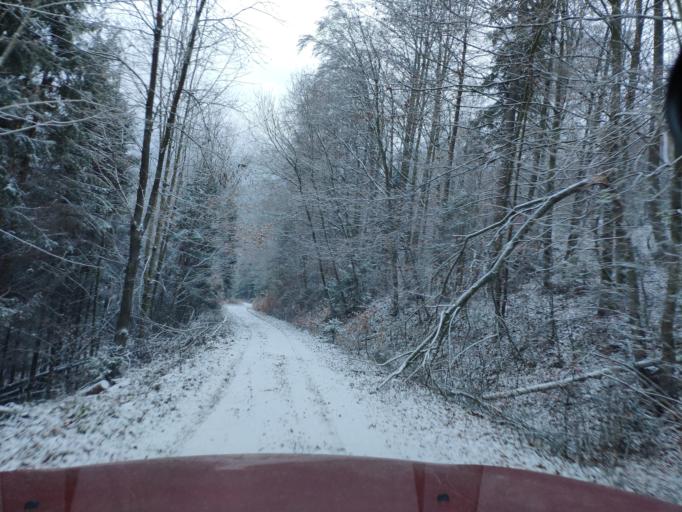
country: SK
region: Kosicky
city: Spisska Nova Ves
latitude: 48.8144
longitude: 20.5135
